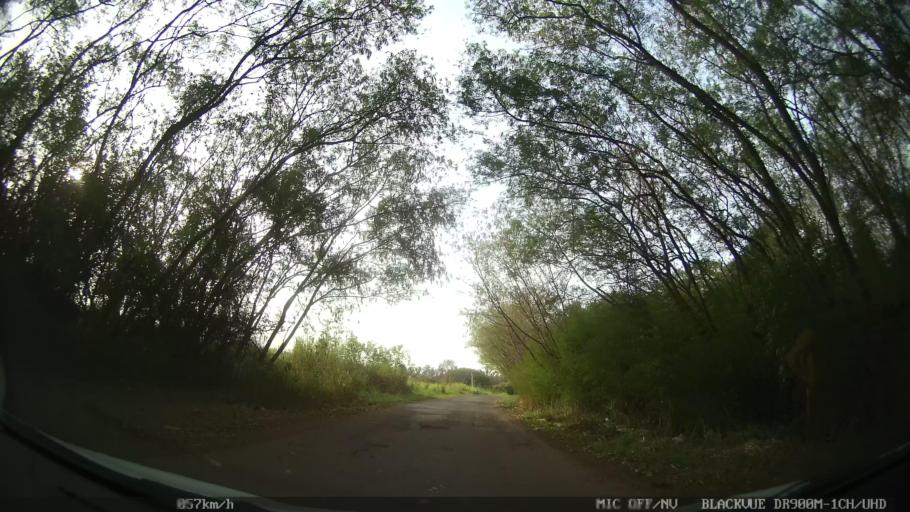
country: BR
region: Sao Paulo
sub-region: Piracicaba
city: Piracicaba
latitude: -22.6982
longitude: -47.5880
